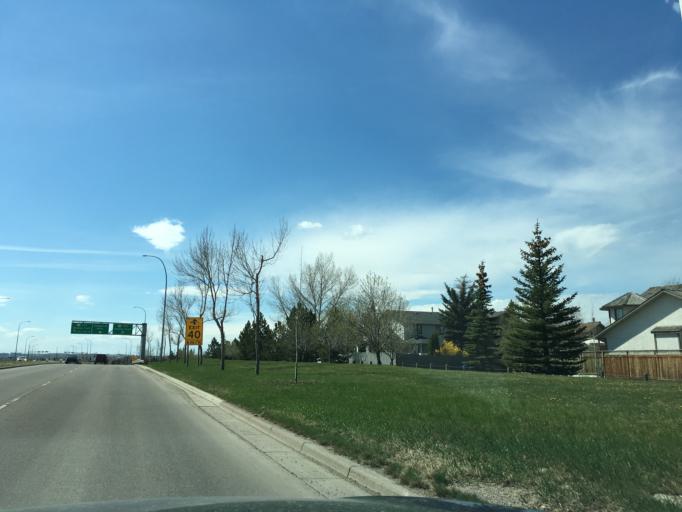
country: CA
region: Alberta
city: Calgary
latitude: 50.8983
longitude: -114.0247
